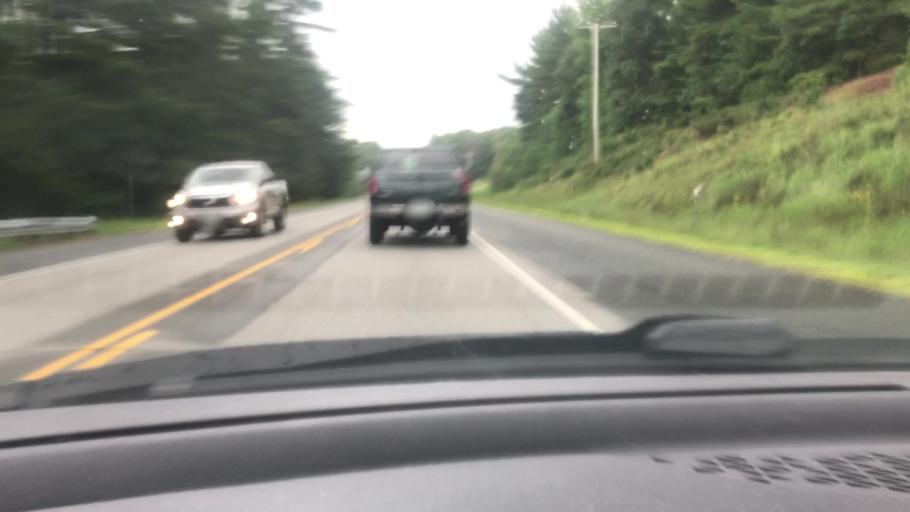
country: US
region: New Hampshire
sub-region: Merrimack County
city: Chichester
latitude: 43.2493
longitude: -71.4617
